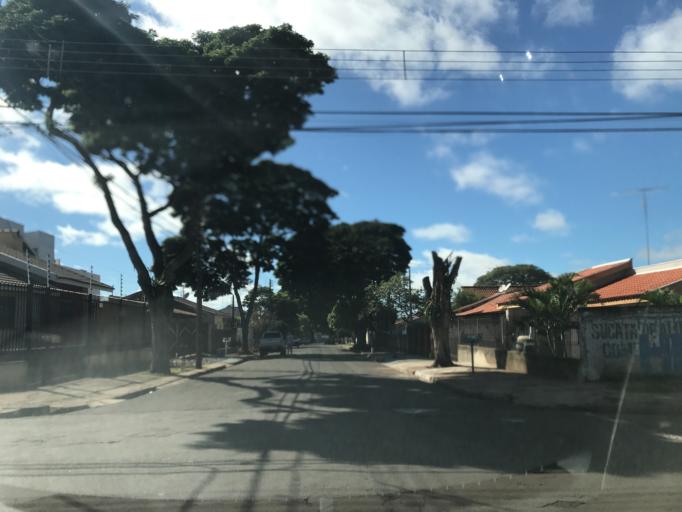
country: BR
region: Parana
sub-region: Maringa
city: Maringa
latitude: -23.4504
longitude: -51.9571
